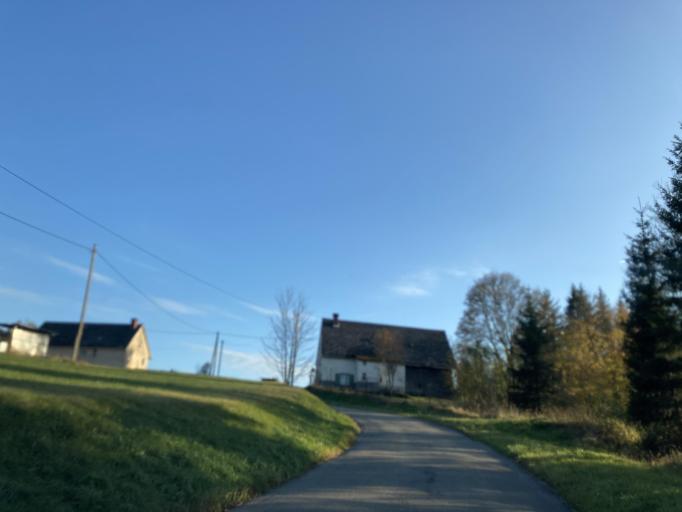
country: DE
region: Baden-Wuerttemberg
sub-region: Freiburg Region
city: Braunlingen
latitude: 47.9871
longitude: 8.3835
